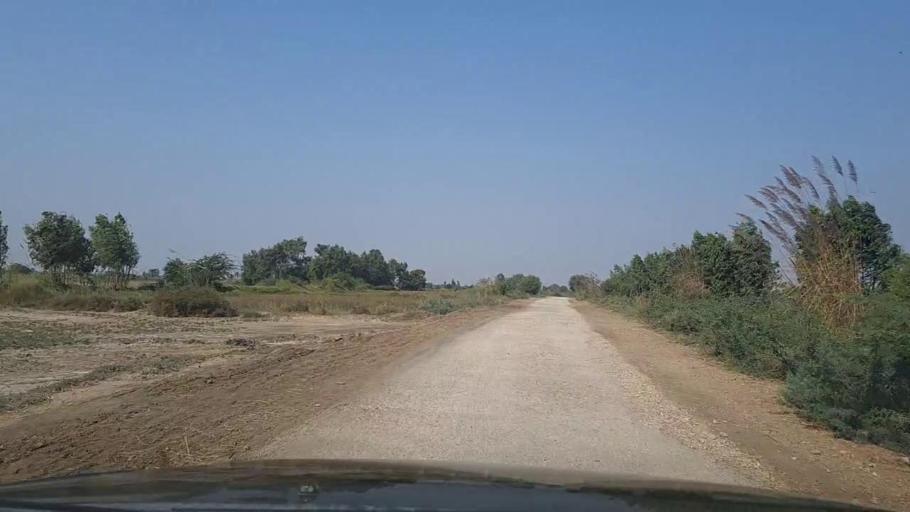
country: PK
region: Sindh
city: Thatta
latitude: 24.6183
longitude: 67.8169
